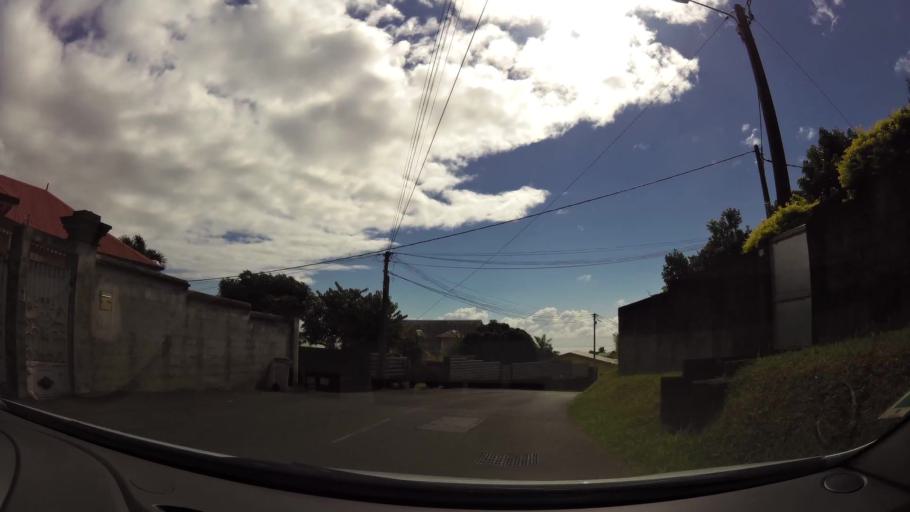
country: RE
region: Reunion
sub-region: Reunion
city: Saint-Denis
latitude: -20.9249
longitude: 55.4902
